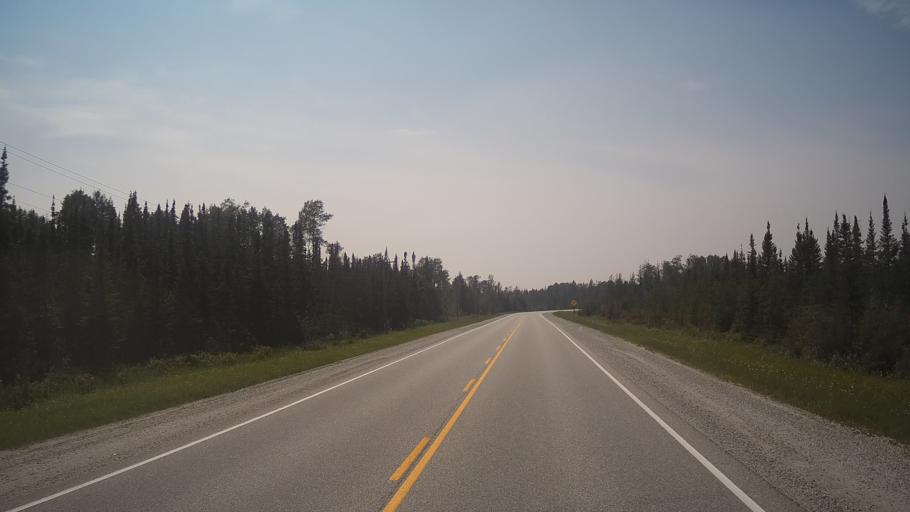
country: CA
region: Ontario
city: Kapuskasing
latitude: 49.2759
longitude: -81.7268
